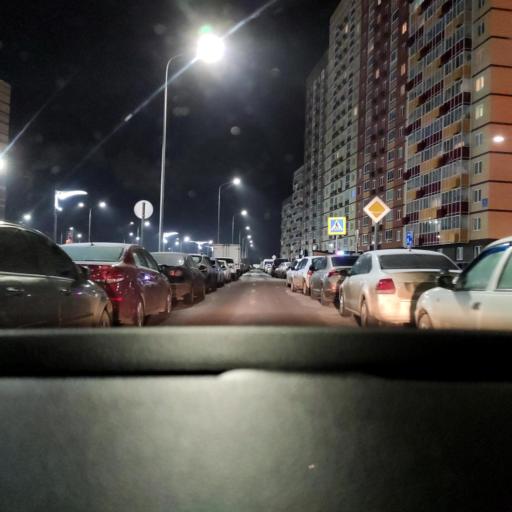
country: RU
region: Moskovskaya
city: Petrovskaya
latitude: 55.5599
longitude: 37.8121
